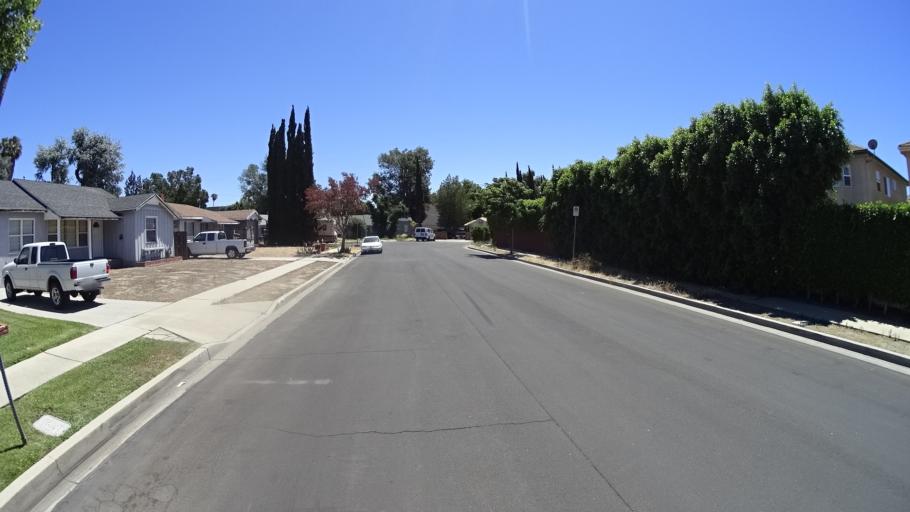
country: US
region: California
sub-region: Los Angeles County
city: San Fernando
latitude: 34.2510
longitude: -118.4694
